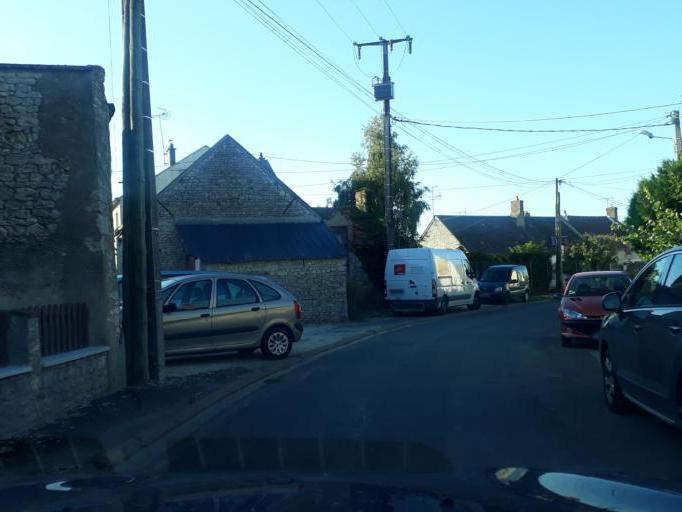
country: FR
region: Centre
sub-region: Departement du Loir-et-Cher
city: Ouzouer-le-Marche
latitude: 47.9704
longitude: 1.5393
